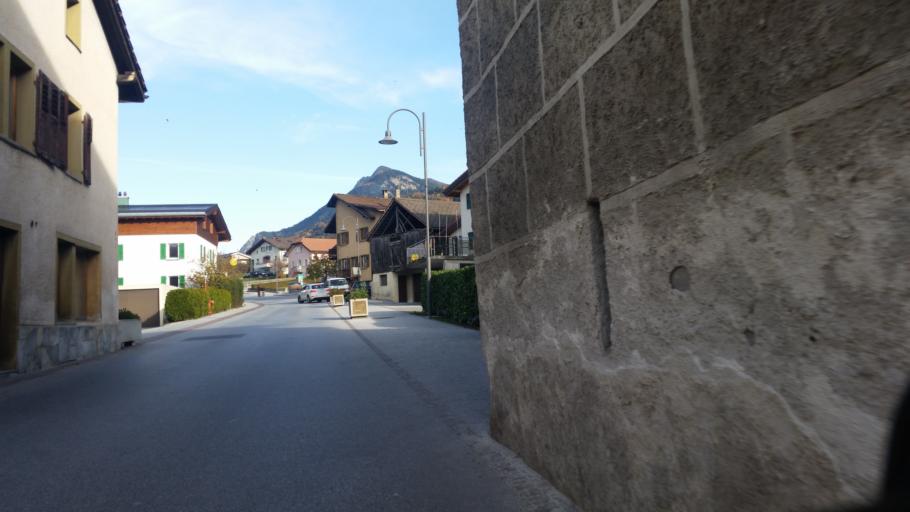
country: CH
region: Valais
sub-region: Sierre District
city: Chalais
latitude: 46.2617
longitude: 7.4959
